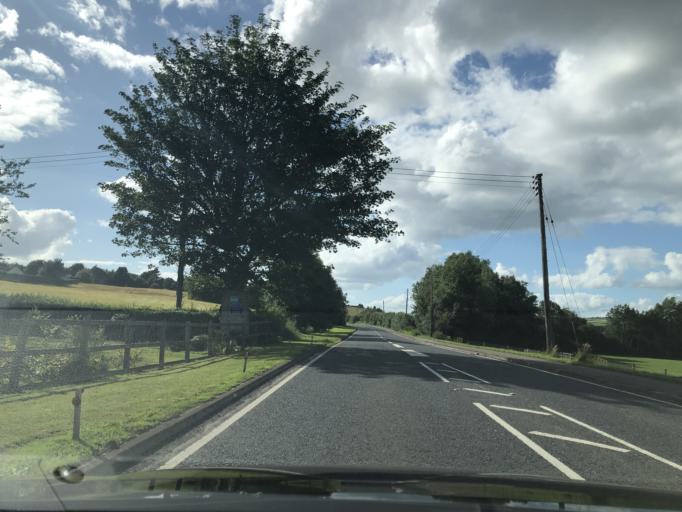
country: GB
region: Northern Ireland
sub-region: Castlereagh District
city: Dundonald
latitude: 54.5773
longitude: -5.7866
